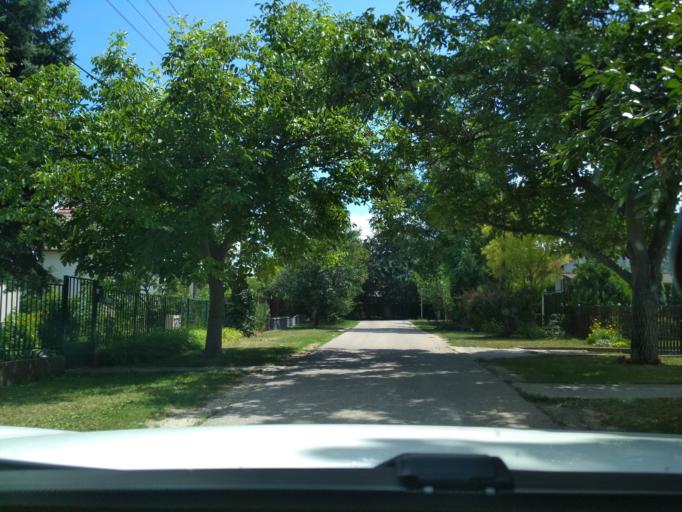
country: HU
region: Fejer
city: Velence
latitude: 47.2247
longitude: 18.6640
